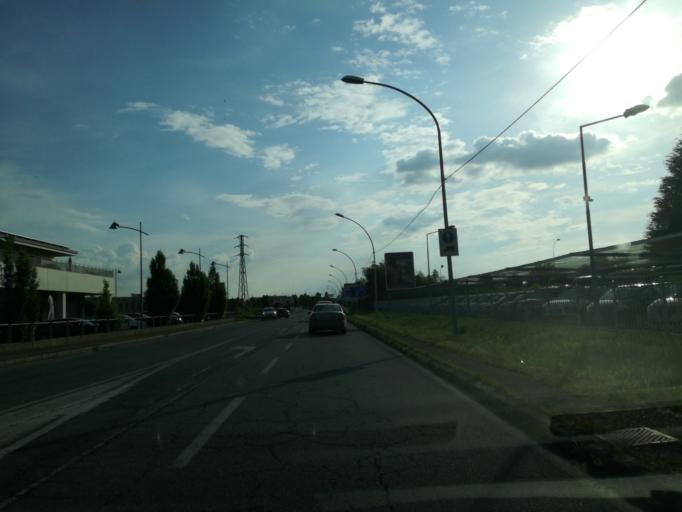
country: IT
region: Lombardy
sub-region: Provincia di Bergamo
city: Calusco d'Adda
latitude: 45.6866
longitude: 9.4633
